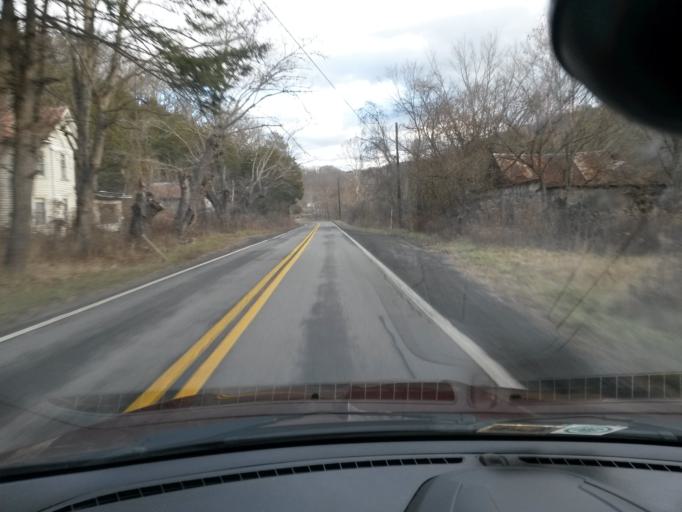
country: US
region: West Virginia
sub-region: Monroe County
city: Union
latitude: 37.5472
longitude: -80.5841
